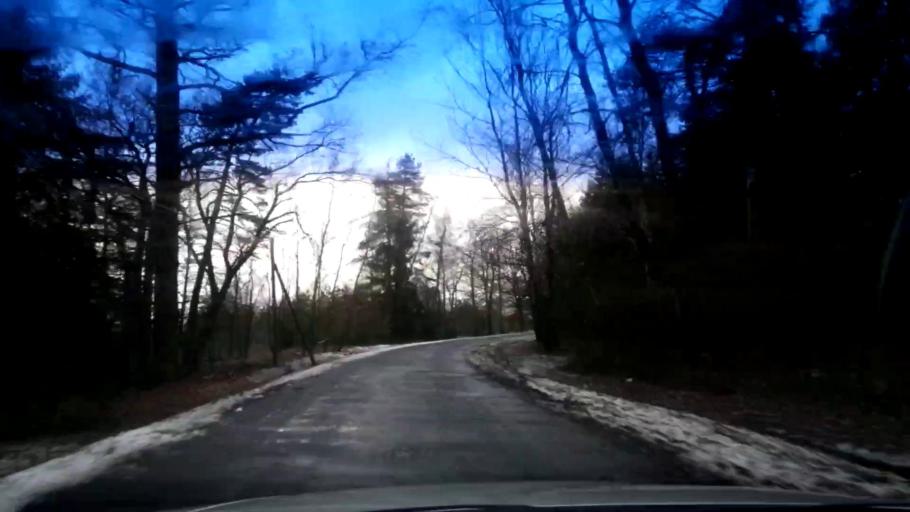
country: CZ
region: Karlovarsky
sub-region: Okres Cheb
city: Cheb
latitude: 50.0436
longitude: 12.3594
